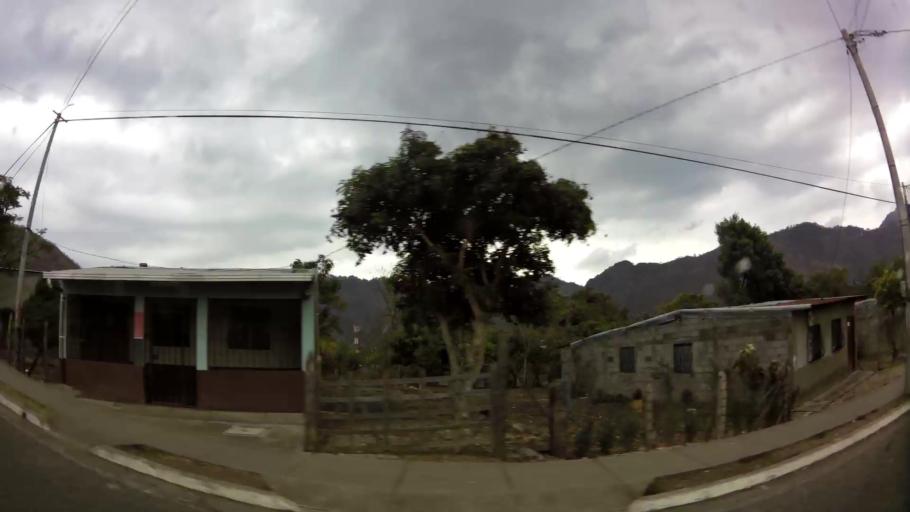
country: NI
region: Jinotega
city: Jinotega
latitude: 13.0948
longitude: -86.0065
